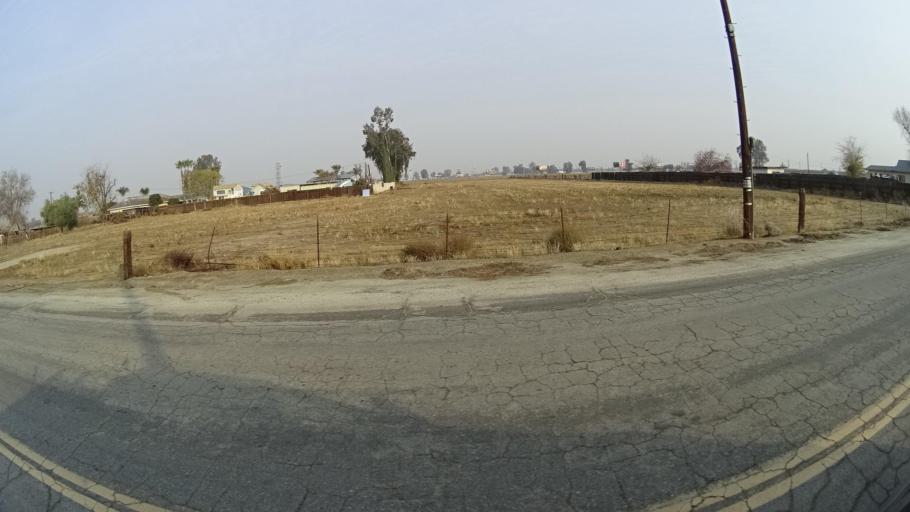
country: US
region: California
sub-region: Kern County
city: Greenfield
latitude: 35.2595
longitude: -119.0246
